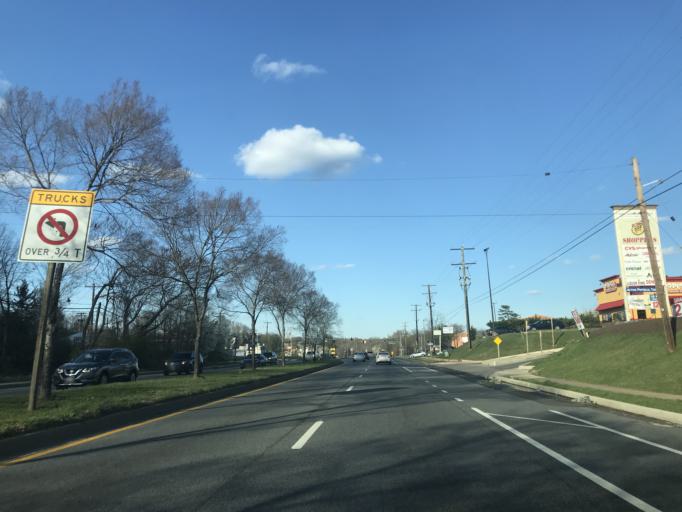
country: US
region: Maryland
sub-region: Prince George's County
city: Peppermill Village
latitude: 38.9151
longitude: -76.8846
